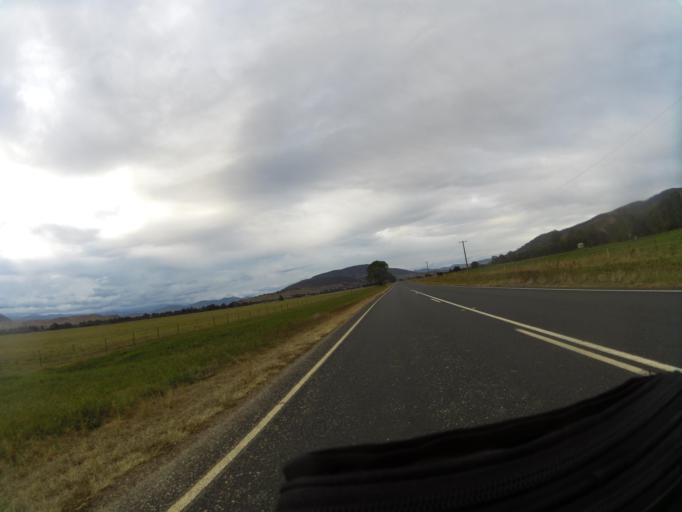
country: AU
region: New South Wales
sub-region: Snowy River
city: Jindabyne
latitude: -36.0949
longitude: 147.9821
